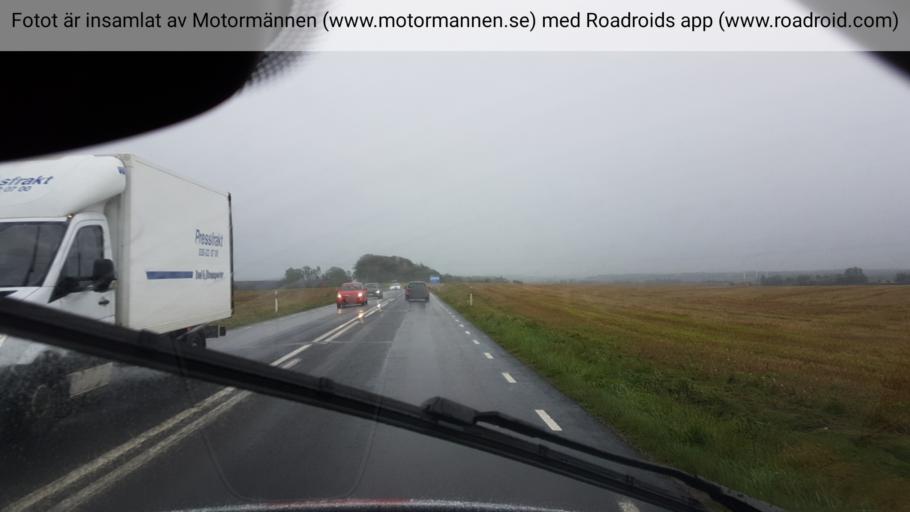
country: SE
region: Halland
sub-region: Halmstads Kommun
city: Paarp
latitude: 56.5923
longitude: 12.9805
